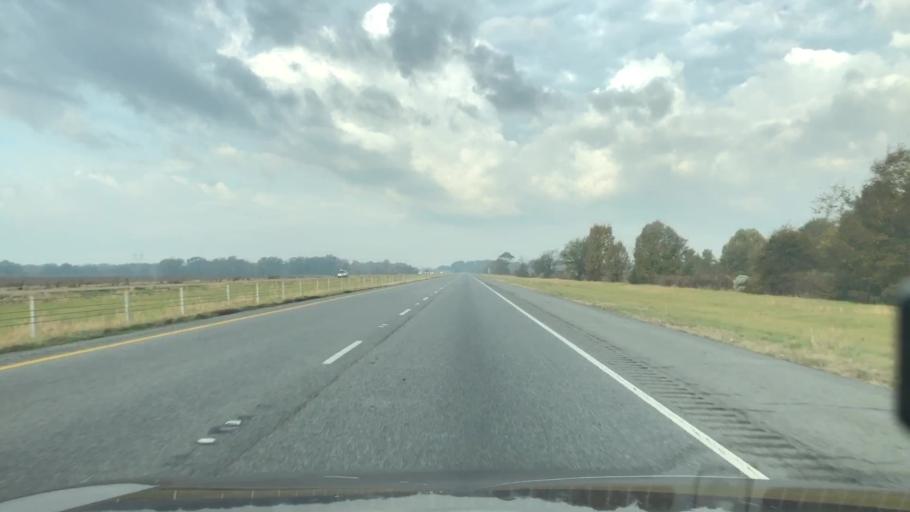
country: US
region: Louisiana
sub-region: Madison Parish
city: Tallulah
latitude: 32.4162
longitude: -91.2810
